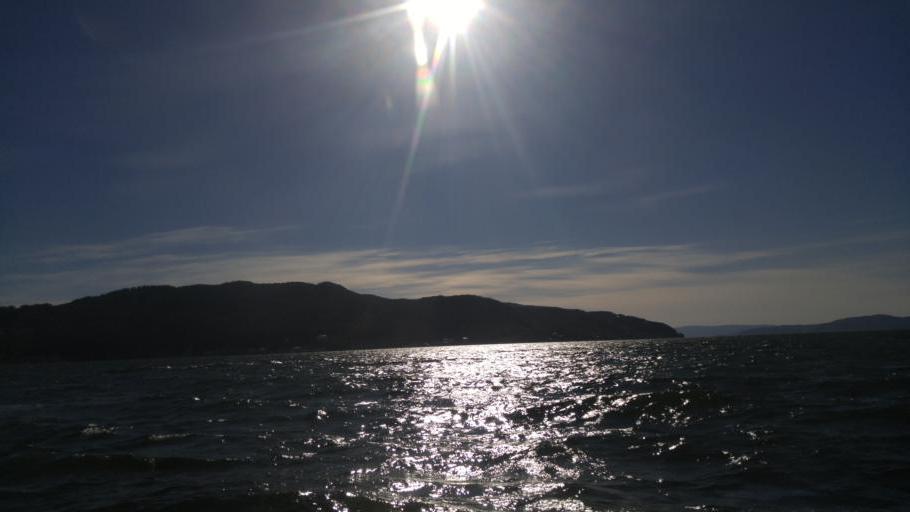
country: NO
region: Sor-Trondelag
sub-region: Trondheim
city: Trondheim
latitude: 63.4456
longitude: 10.3902
